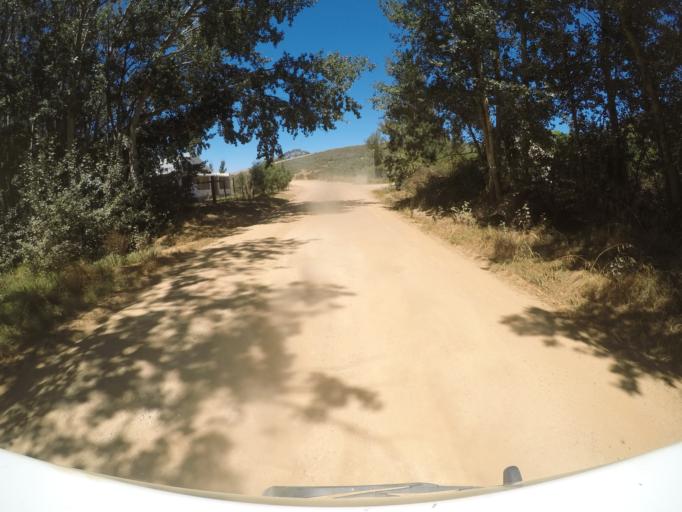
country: ZA
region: Western Cape
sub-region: Overberg District Municipality
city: Grabouw
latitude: -34.0954
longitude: 19.1974
